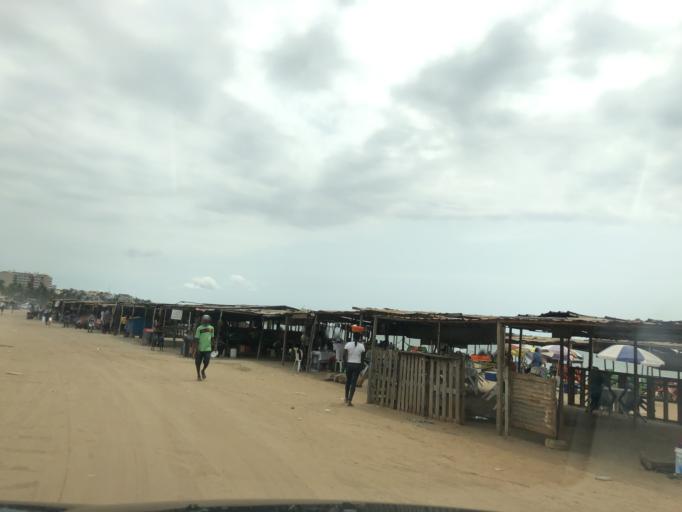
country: AO
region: Luanda
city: Luanda
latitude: -8.8715
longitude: 13.1944
